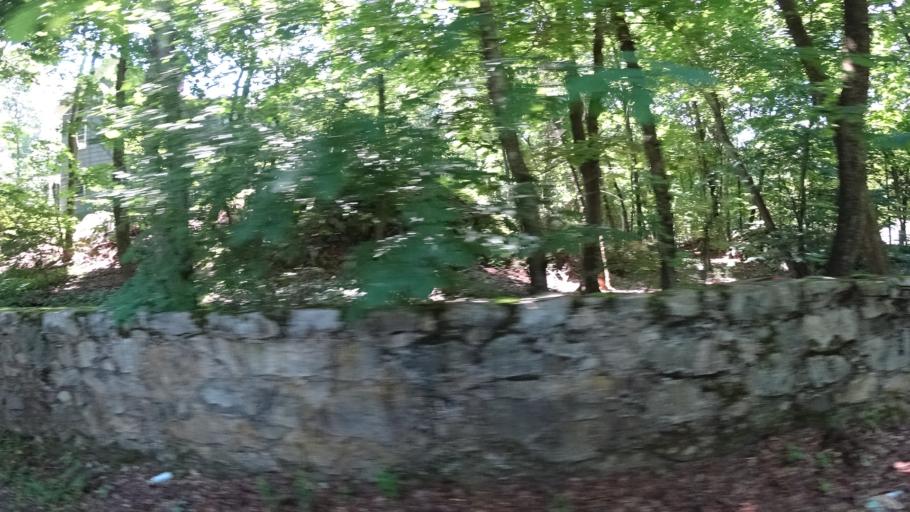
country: US
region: Massachusetts
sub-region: Norfolk County
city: Dedham
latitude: 42.2540
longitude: -71.1916
